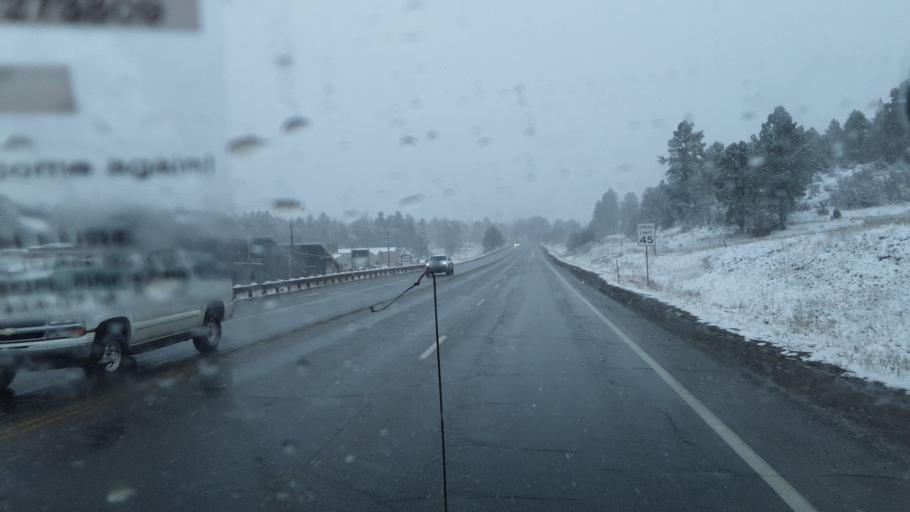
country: US
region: Colorado
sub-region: Archuleta County
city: Pagosa Springs
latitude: 37.2690
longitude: -107.0297
